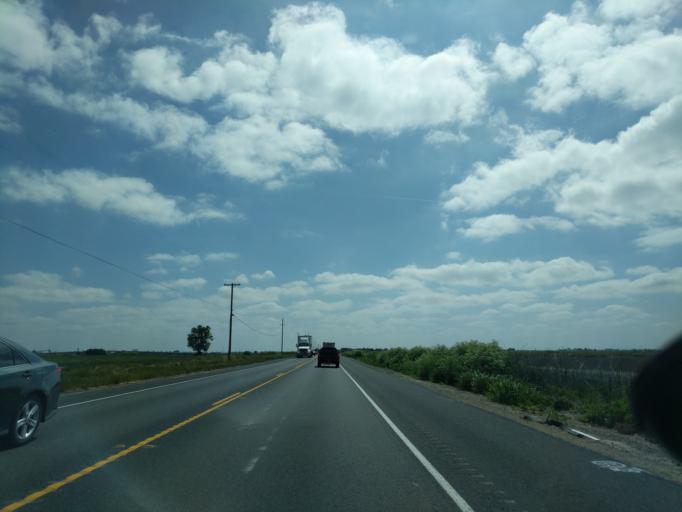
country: US
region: California
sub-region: San Joaquin County
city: Country Club
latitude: 37.9268
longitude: -121.3798
